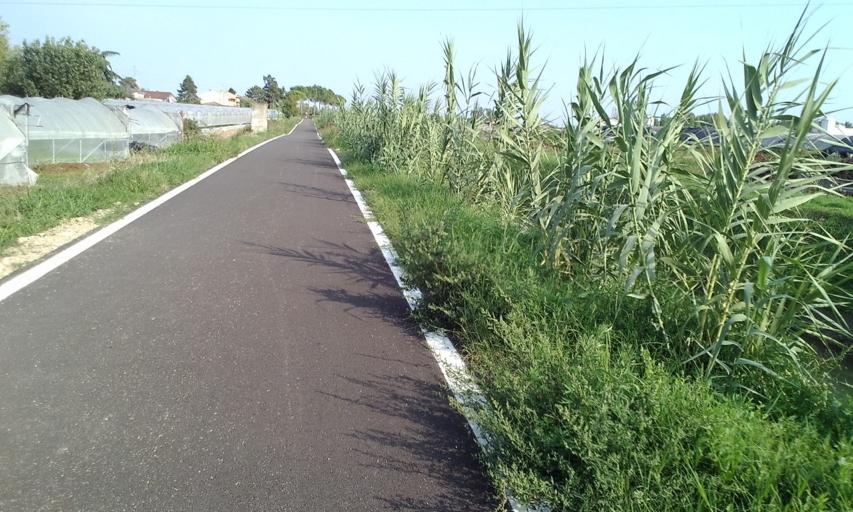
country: IT
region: Veneto
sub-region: Provincia di Verona
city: Raldon
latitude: 45.3539
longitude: 11.0188
